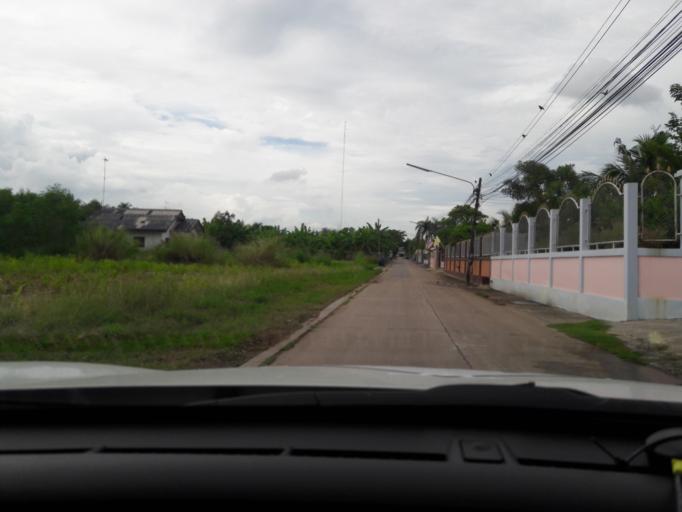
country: TH
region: Nakhon Sawan
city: Tak Fa
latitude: 15.3468
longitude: 100.5022
